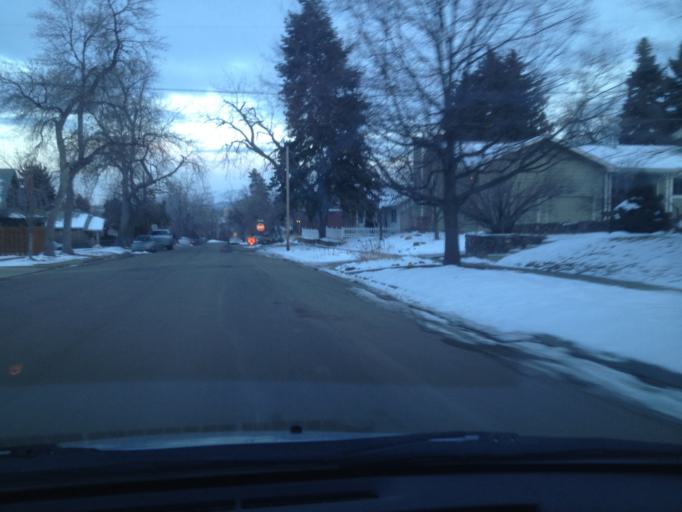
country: US
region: Colorado
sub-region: Jefferson County
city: Golden
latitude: 39.7616
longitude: -105.2288
